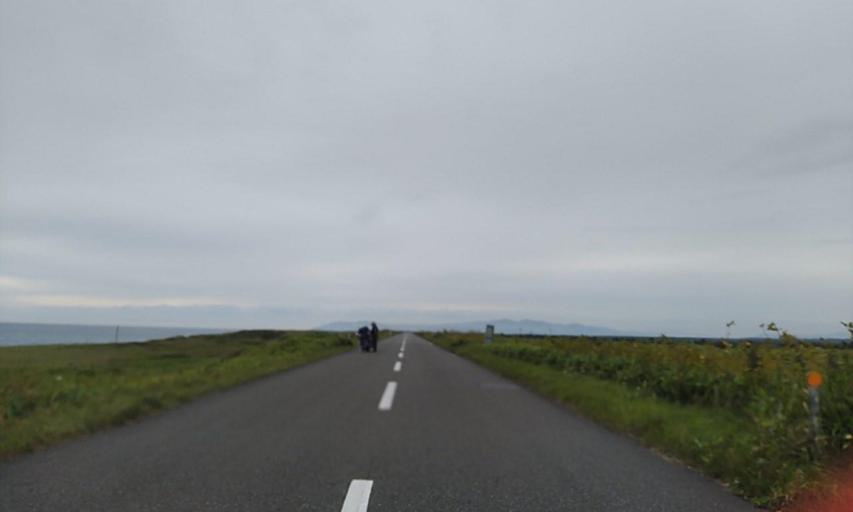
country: JP
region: Hokkaido
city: Makubetsu
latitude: 45.2687
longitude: 142.2384
